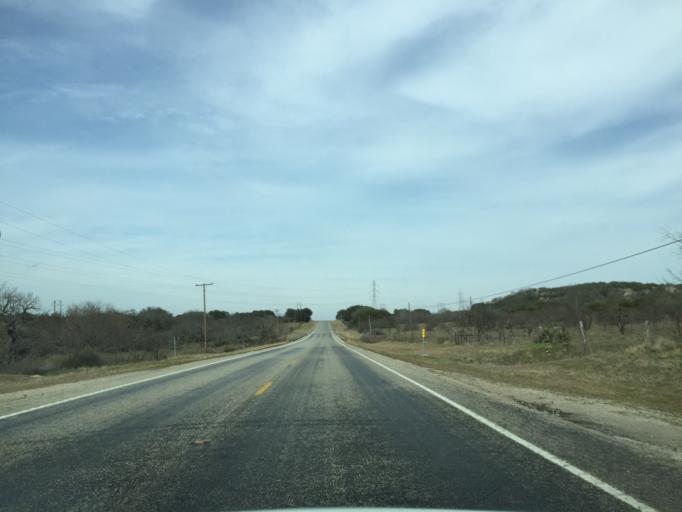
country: US
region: Texas
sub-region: Gillespie County
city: Fredericksburg
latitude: 30.4438
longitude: -98.7354
